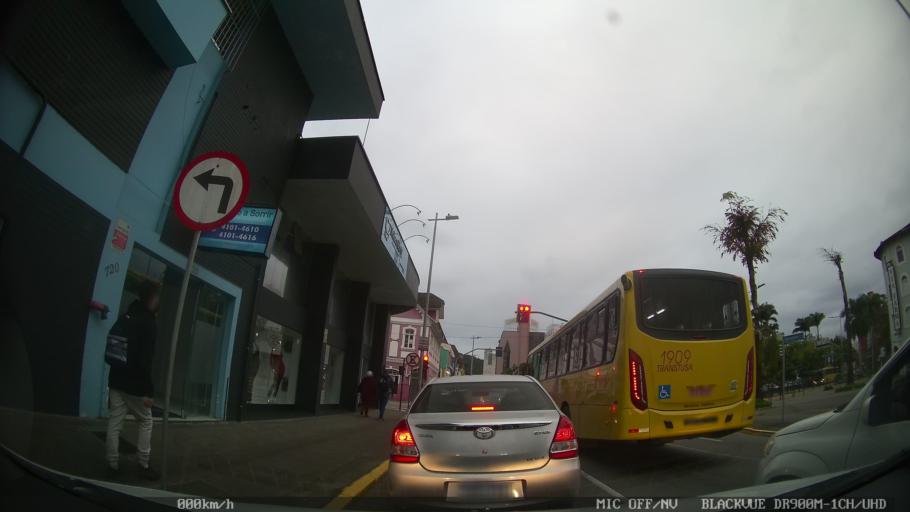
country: BR
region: Santa Catarina
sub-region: Joinville
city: Joinville
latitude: -26.3015
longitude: -48.8483
